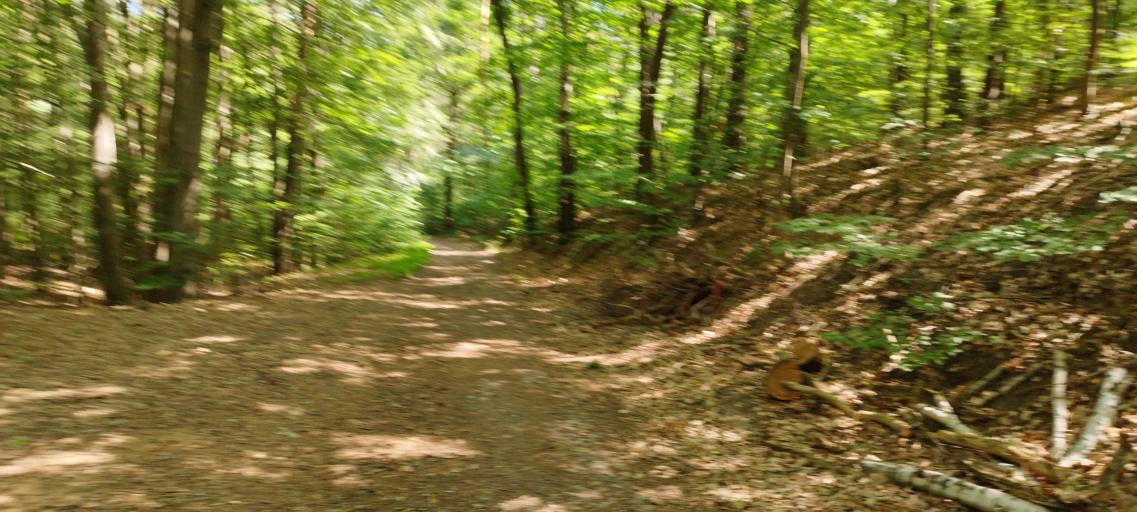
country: DE
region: Brandenburg
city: Rauen
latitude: 52.3205
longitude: 14.0240
